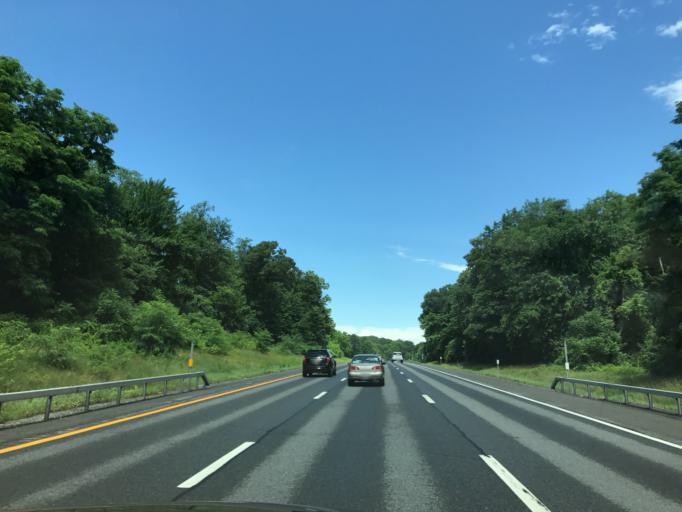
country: US
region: New York
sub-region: Saratoga County
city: Country Knolls
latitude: 42.9139
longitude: -73.7949
